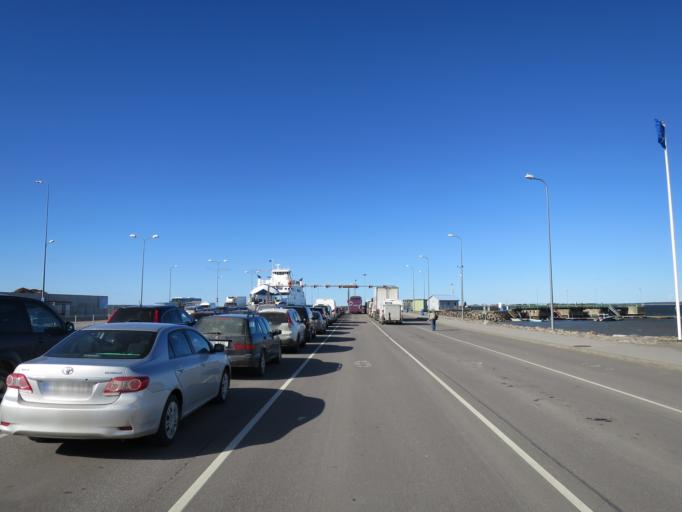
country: EE
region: Laeaene
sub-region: Lihula vald
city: Lihula
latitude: 58.5736
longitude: 23.5106
